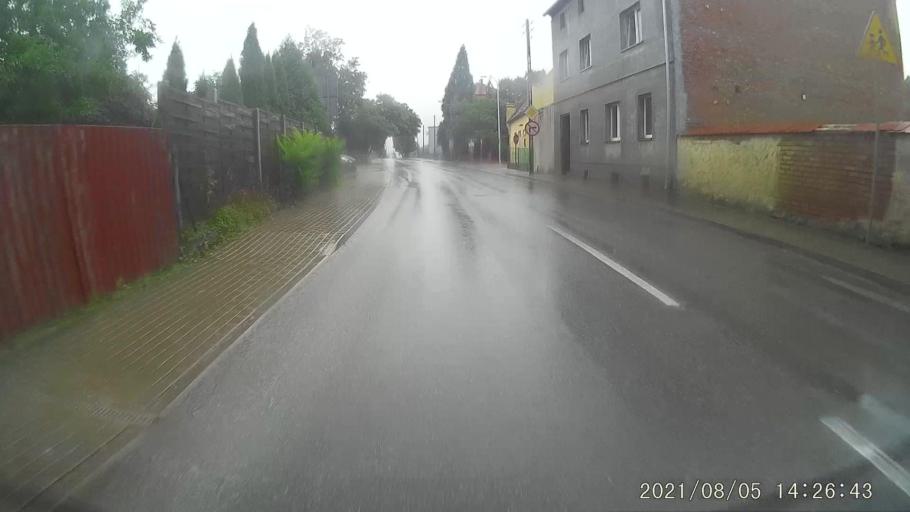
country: PL
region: Opole Voivodeship
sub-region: Powiat nyski
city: Korfantow
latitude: 50.4891
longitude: 17.5983
